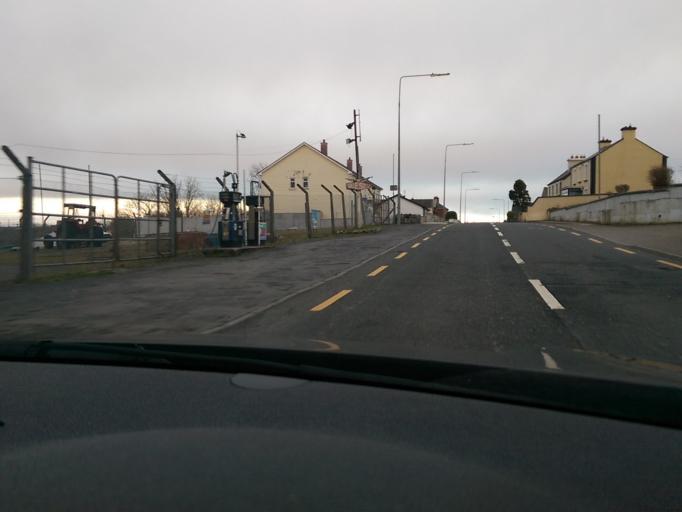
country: IE
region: Connaught
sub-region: Sligo
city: Ballymote
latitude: 53.9952
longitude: -8.5207
